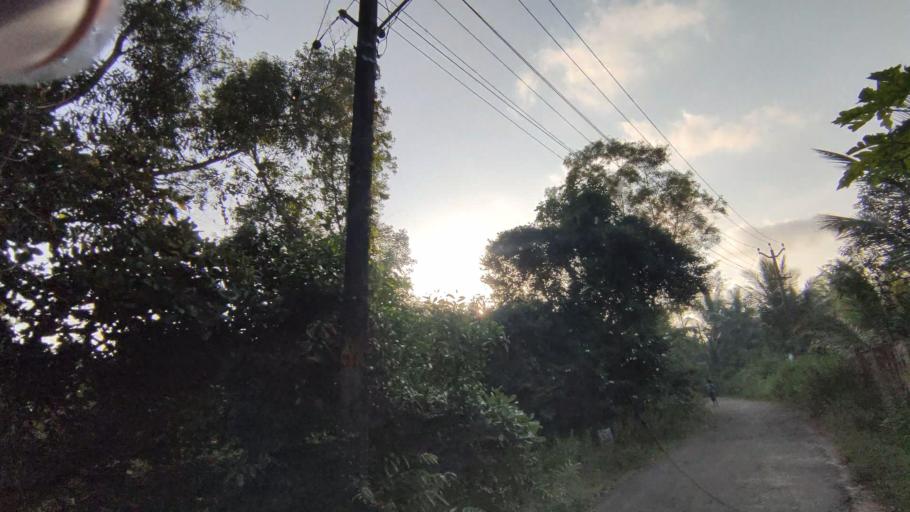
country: IN
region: Kerala
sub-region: Alappuzha
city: Shertallai
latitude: 9.6507
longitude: 76.3542
